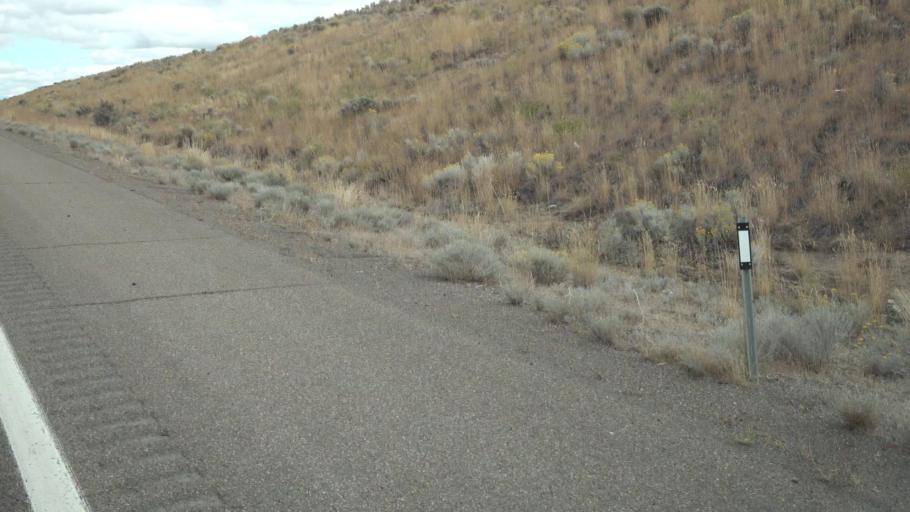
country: US
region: Nevada
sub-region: Elko County
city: Elko
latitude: 40.8954
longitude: -115.7096
